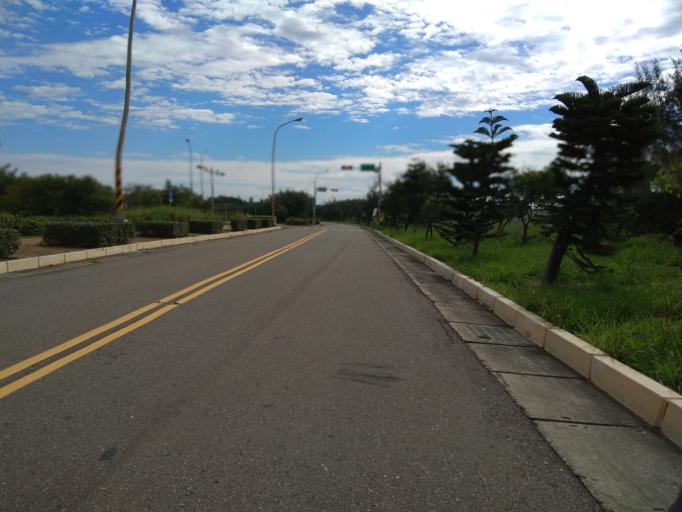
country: TW
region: Taiwan
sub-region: Hsinchu
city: Zhubei
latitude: 25.0456
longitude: 121.0807
